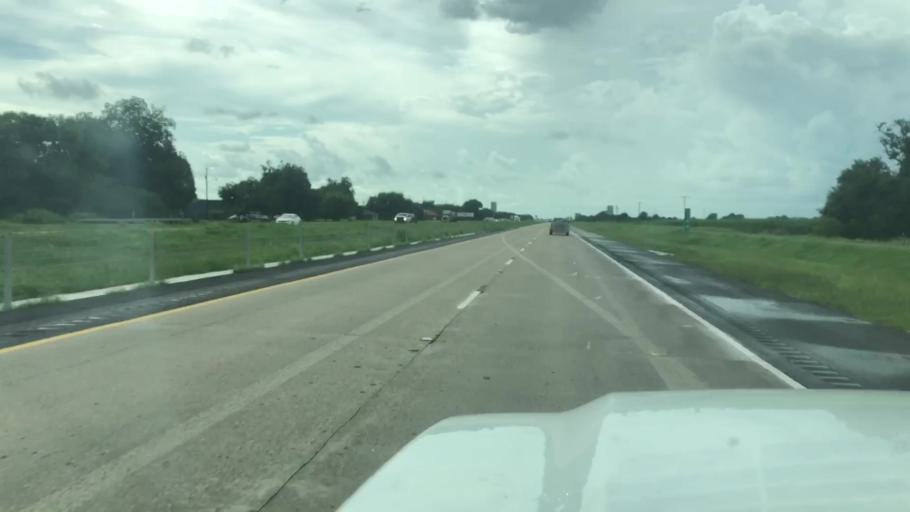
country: US
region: Louisiana
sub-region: Iberia Parish
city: Jeanerette
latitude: 29.8709
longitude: -91.6421
